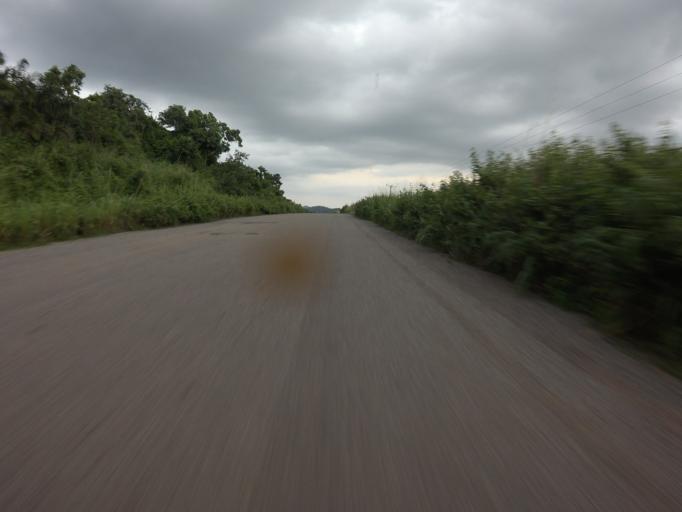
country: GH
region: Volta
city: Ho
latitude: 6.7881
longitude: 0.3679
